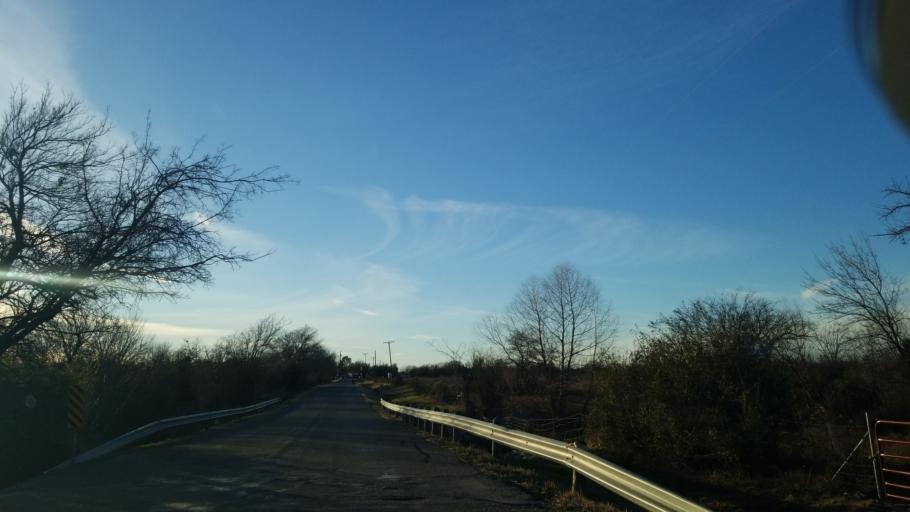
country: US
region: Texas
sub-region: Denton County
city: Denton
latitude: 33.1832
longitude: -97.1513
